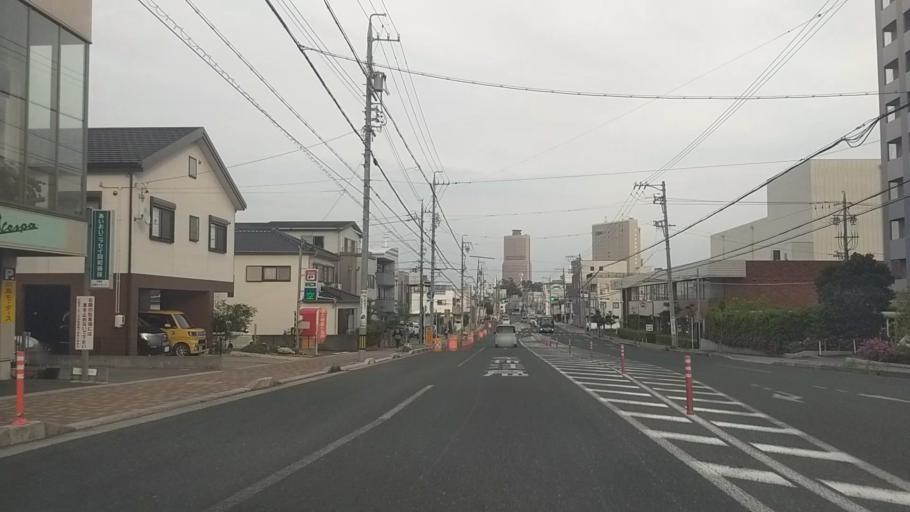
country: JP
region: Shizuoka
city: Hamamatsu
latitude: 34.7183
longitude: 137.7231
